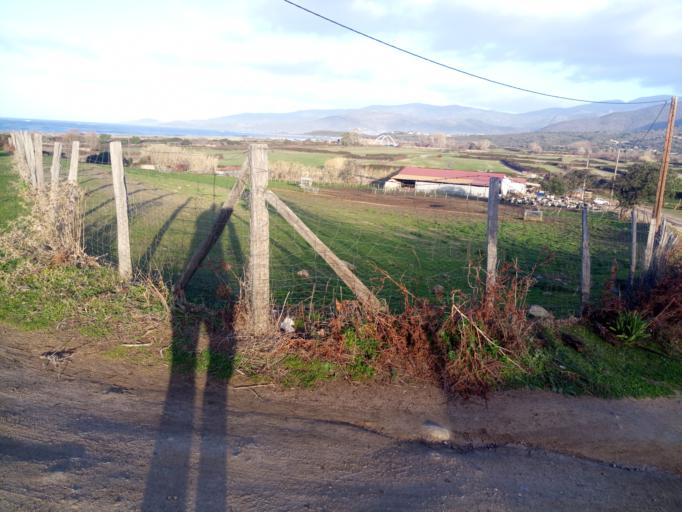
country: FR
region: Corsica
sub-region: Departement de la Corse-du-Sud
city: Appietto
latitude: 42.0703
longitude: 8.7272
